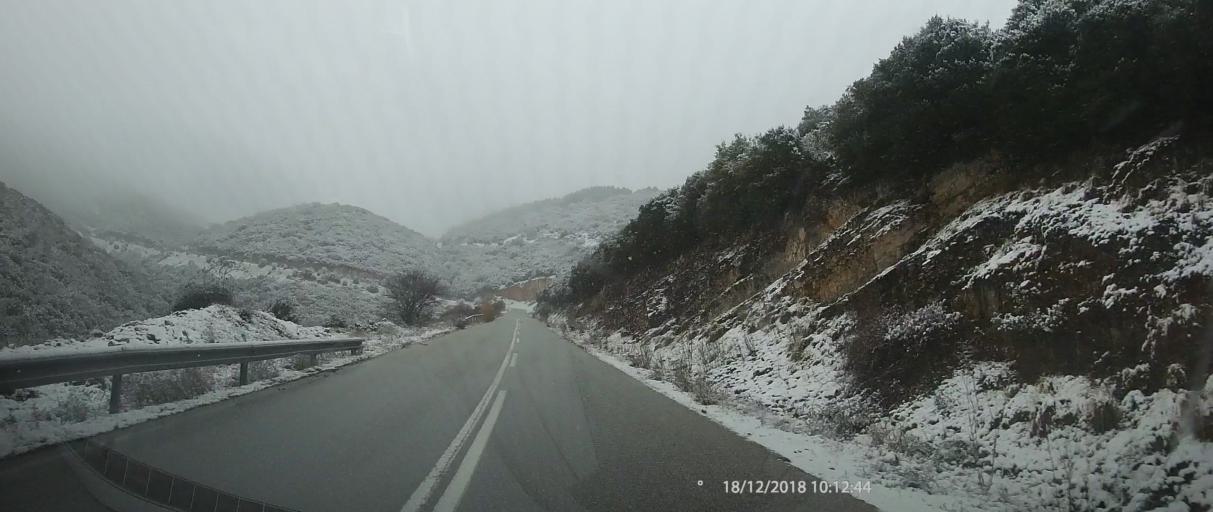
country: GR
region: Thessaly
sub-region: Nomos Larisis
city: Livadi
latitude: 40.1011
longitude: 22.2089
